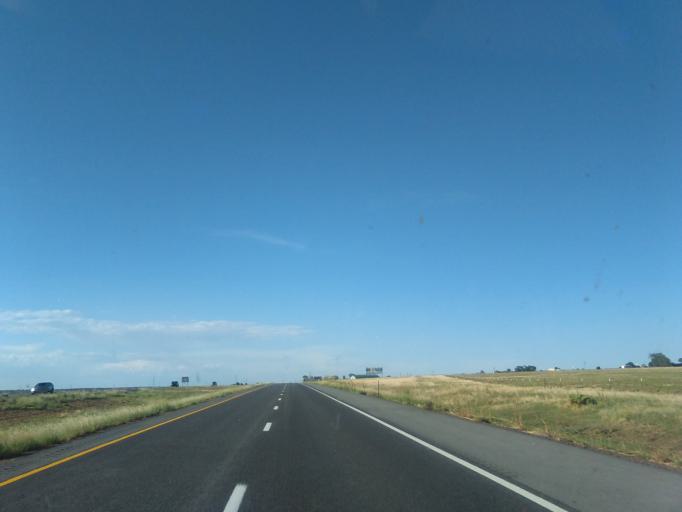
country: US
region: New Mexico
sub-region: San Miguel County
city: Las Vegas
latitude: 35.6491
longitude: -105.1926
